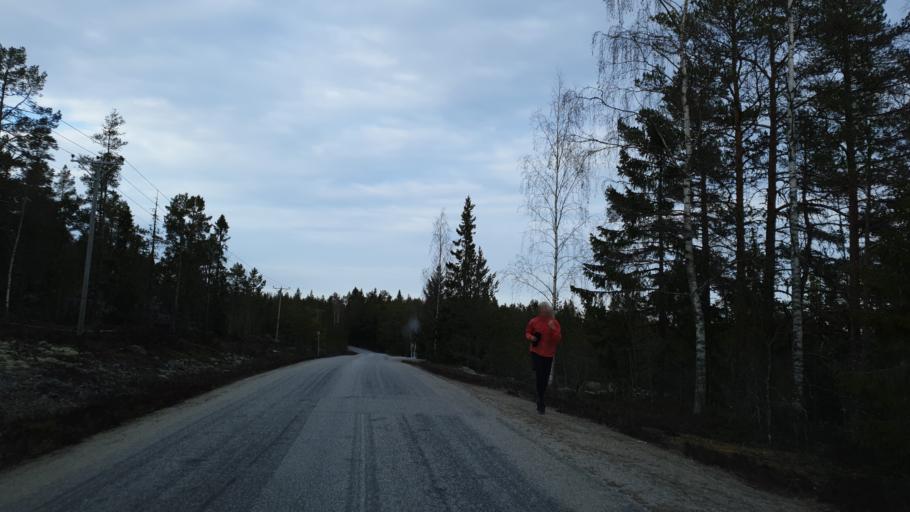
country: SE
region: Vaesternorrland
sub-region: Sundsvalls Kommun
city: Njurundabommen
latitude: 61.9680
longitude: 17.3801
